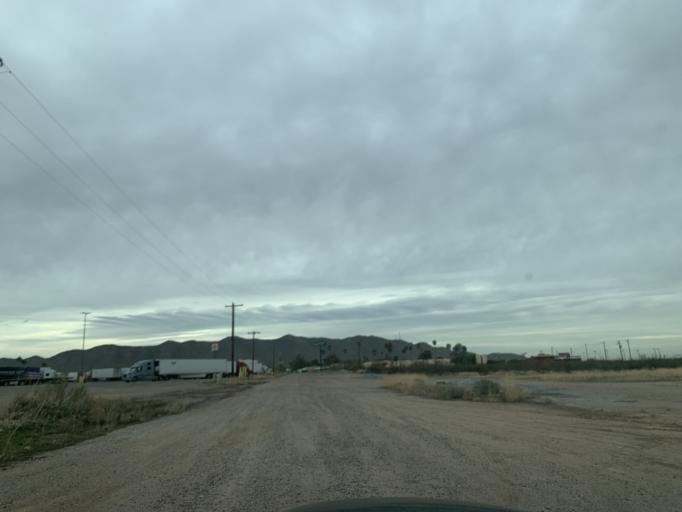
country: US
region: Arizona
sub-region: Pinal County
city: Arizona City
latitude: 32.8139
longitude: -111.6678
